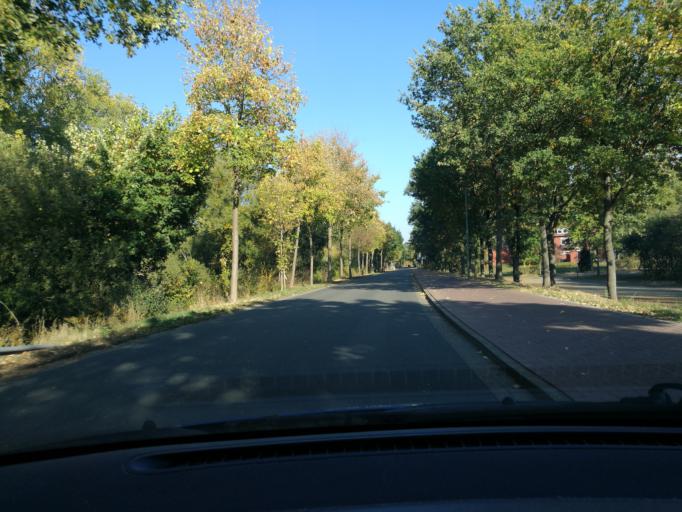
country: DE
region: Lower Saxony
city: Dannenberg
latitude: 53.1008
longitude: 11.0953
